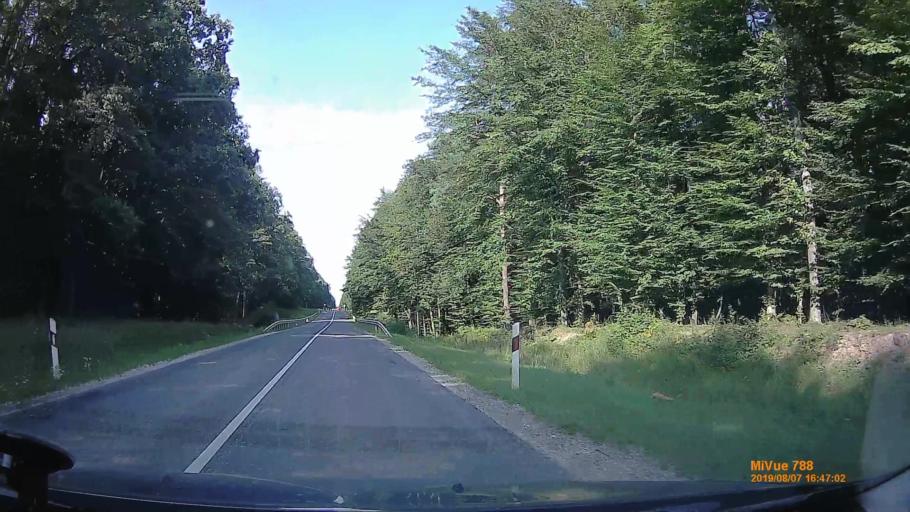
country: HU
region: Zala
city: Lenti
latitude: 46.6581
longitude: 16.6313
